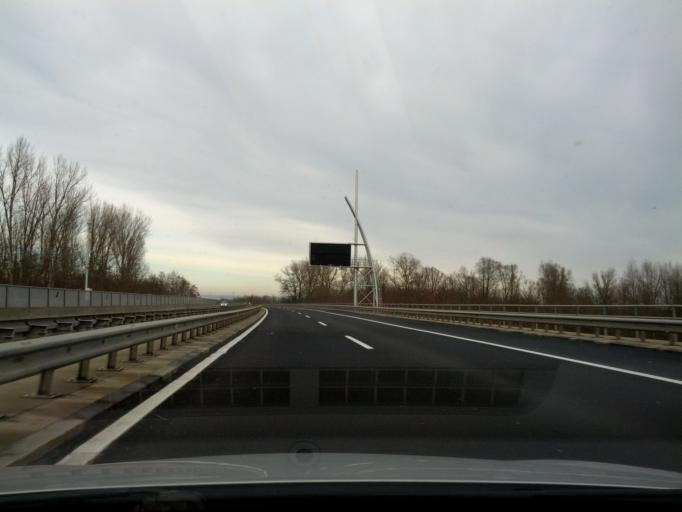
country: SI
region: Murska Sobota
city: Bakovci
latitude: 46.6064
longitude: 16.1284
